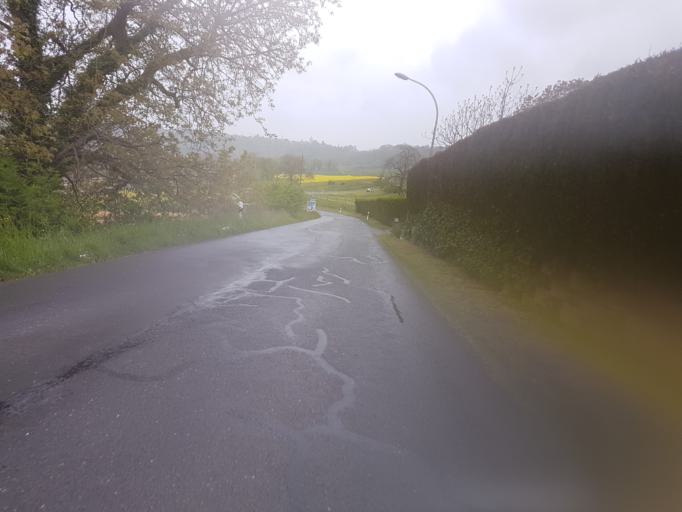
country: CH
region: Vaud
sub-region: Gros-de-Vaud District
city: Penthalaz
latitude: 46.6286
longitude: 6.5245
